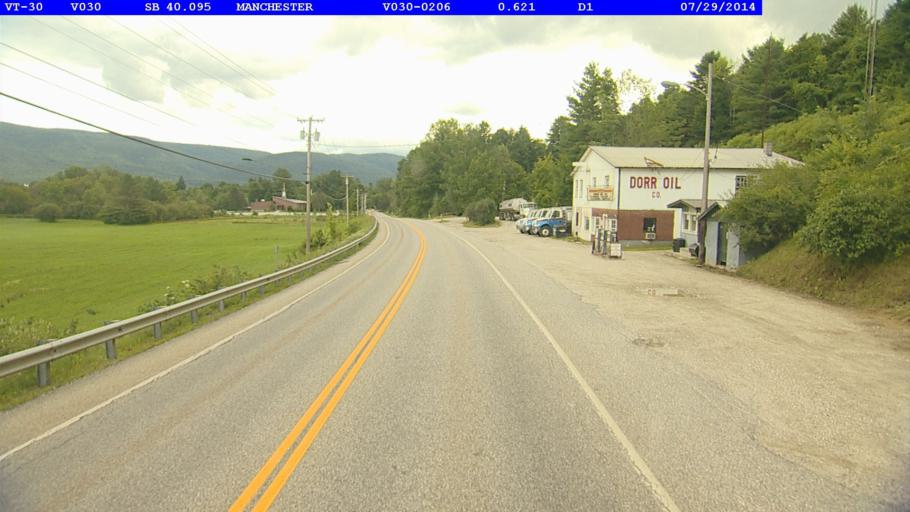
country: US
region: Vermont
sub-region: Bennington County
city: Manchester Center
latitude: 43.1857
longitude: -73.0580
